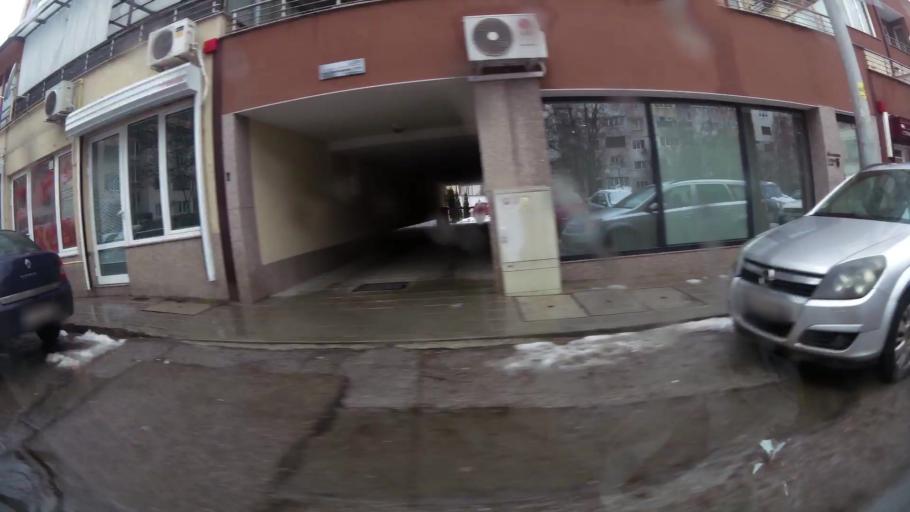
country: BG
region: Sofia-Capital
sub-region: Stolichna Obshtina
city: Sofia
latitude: 42.6685
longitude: 23.2691
